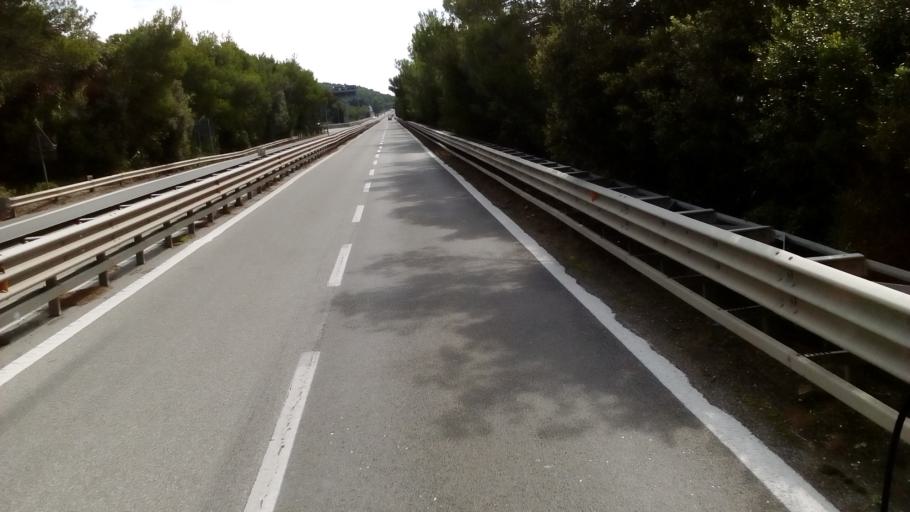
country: IT
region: Tuscany
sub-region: Provincia di Livorno
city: Quercianella
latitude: 43.4440
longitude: 10.3842
